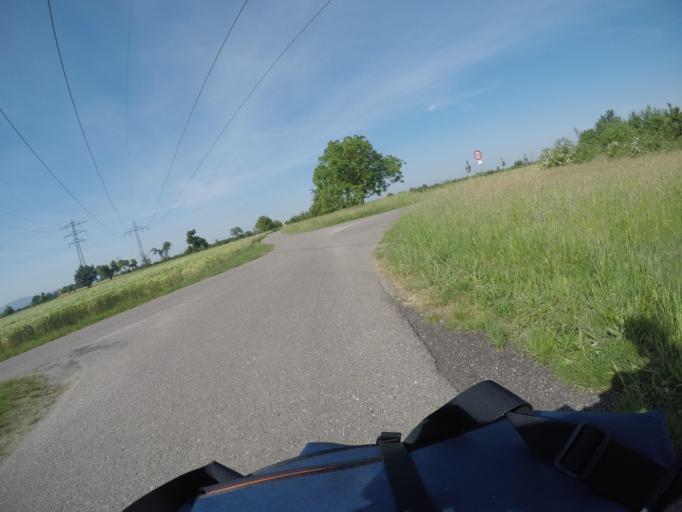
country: DE
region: Baden-Wuerttemberg
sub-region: Karlsruhe Region
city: Bietigheim
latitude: 48.9014
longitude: 8.2722
